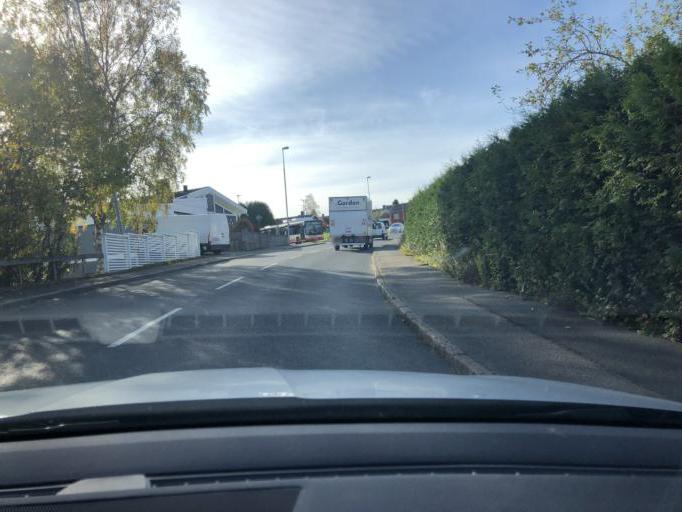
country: SE
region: Joenkoeping
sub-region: Jonkopings Kommun
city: Jonkoping
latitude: 57.7743
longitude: 14.1262
